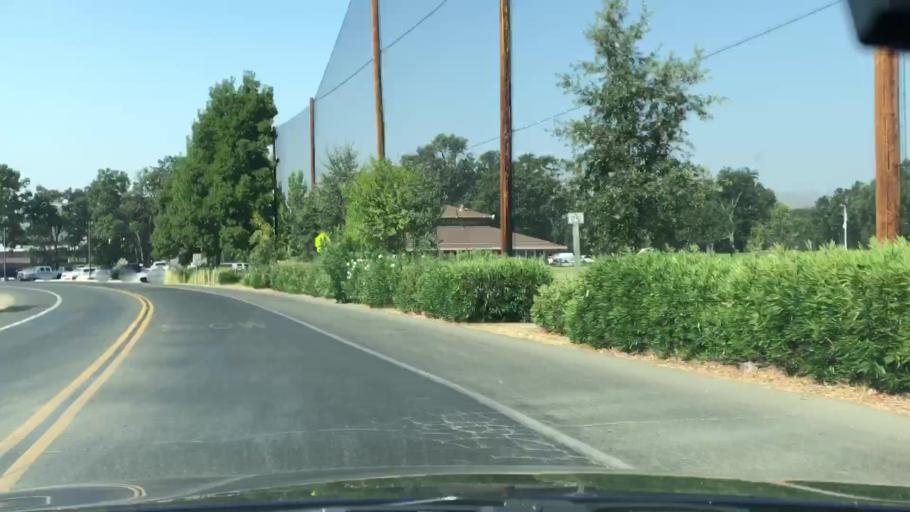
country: US
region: California
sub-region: Lake County
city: Hidden Valley Lake
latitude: 38.7967
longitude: -122.5547
